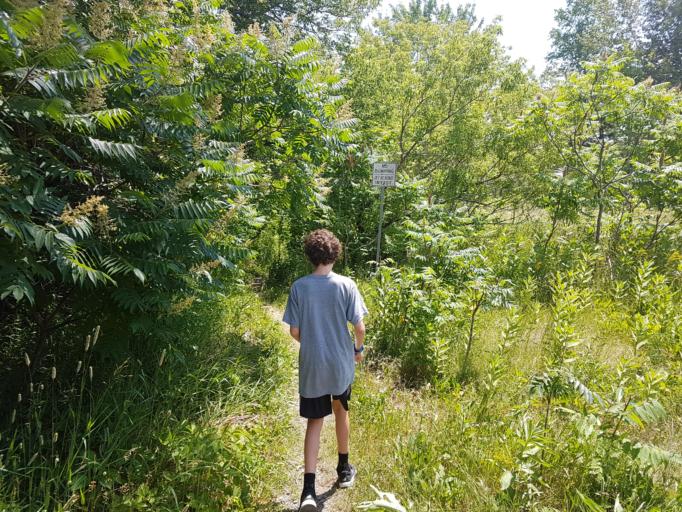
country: CA
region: New Brunswick
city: Fredericton
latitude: 45.9514
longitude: -66.6109
